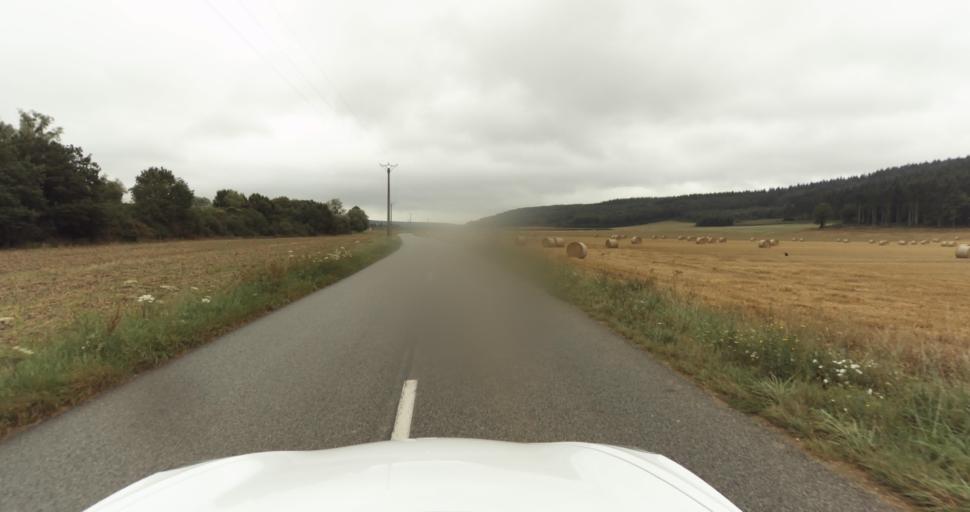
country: FR
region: Haute-Normandie
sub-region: Departement de l'Eure
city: Normanville
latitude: 49.0819
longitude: 1.1404
